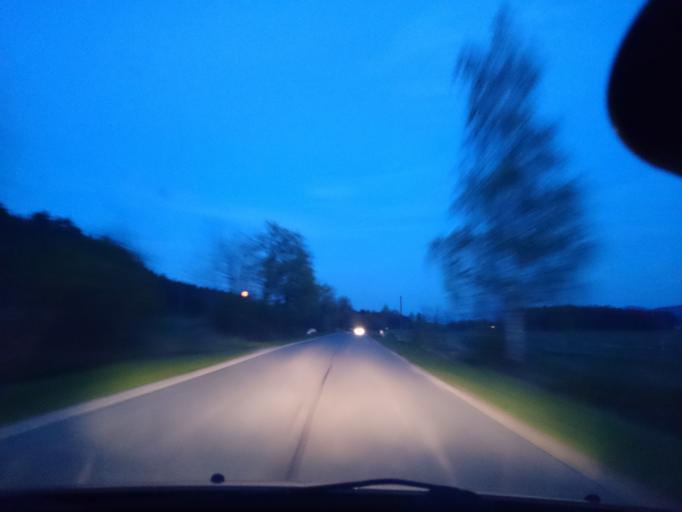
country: PL
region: Lower Silesian Voivodeship
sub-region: Powiat zabkowicki
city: Budzow
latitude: 50.5526
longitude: 16.7124
